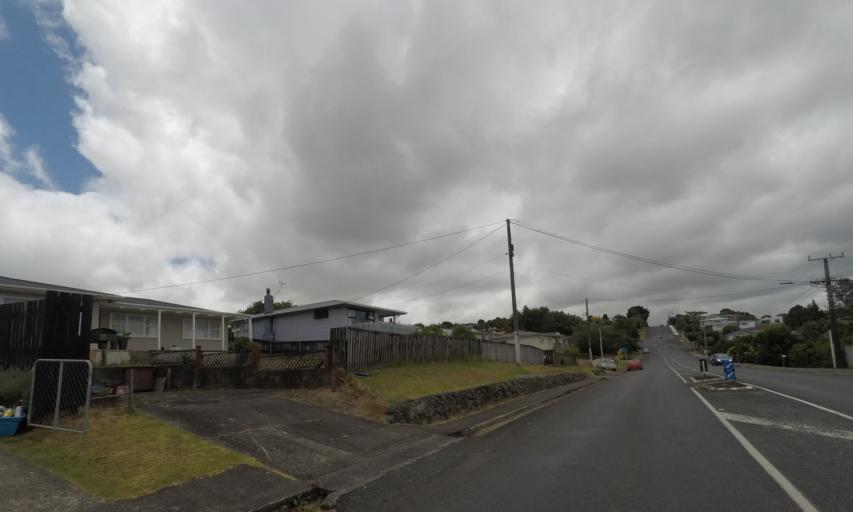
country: NZ
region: Northland
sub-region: Whangarei
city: Whangarei
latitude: -35.6783
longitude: 174.3137
